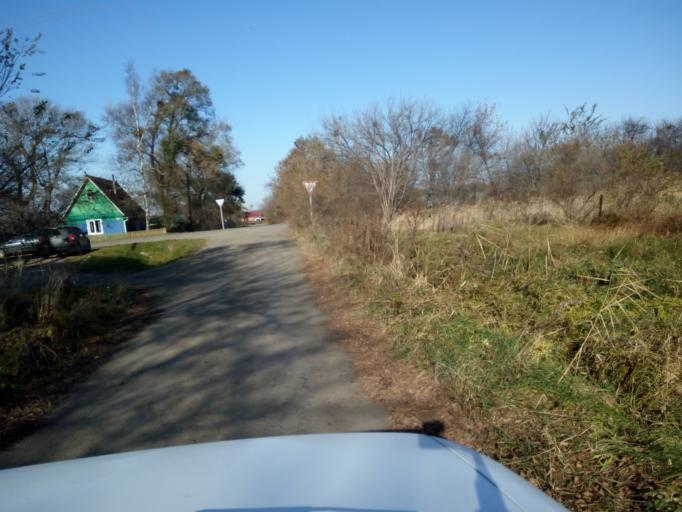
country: RU
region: Primorskiy
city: Lazo
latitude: 45.8700
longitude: 133.6468
